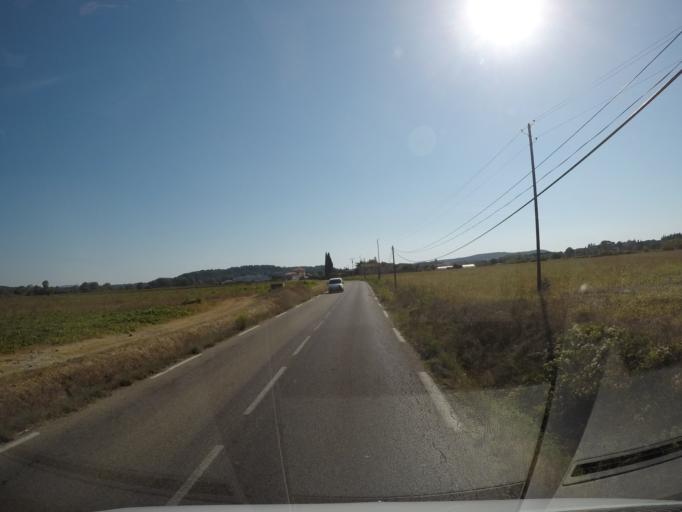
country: FR
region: Languedoc-Roussillon
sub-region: Departement du Gard
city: Ribaute-les-Tavernes
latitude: 44.0232
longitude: 4.0923
